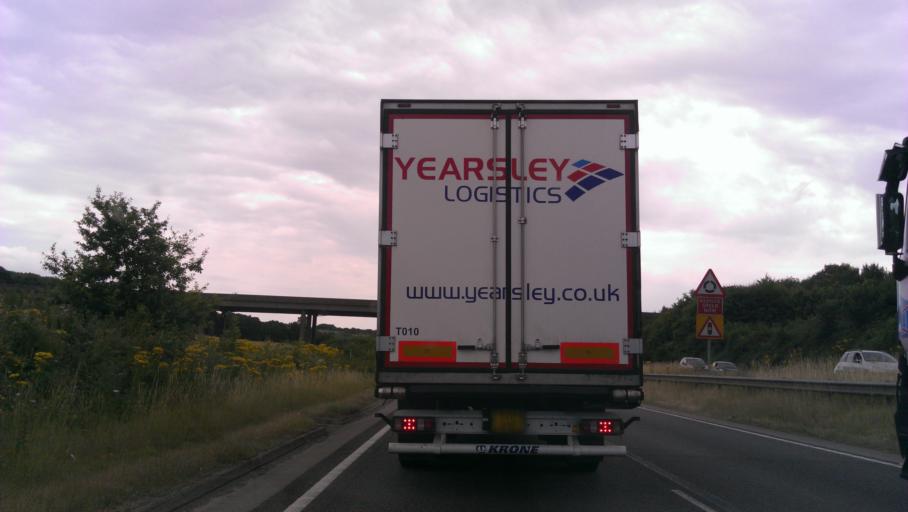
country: GB
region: England
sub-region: Kent
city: Newington
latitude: 51.3318
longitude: 0.6645
